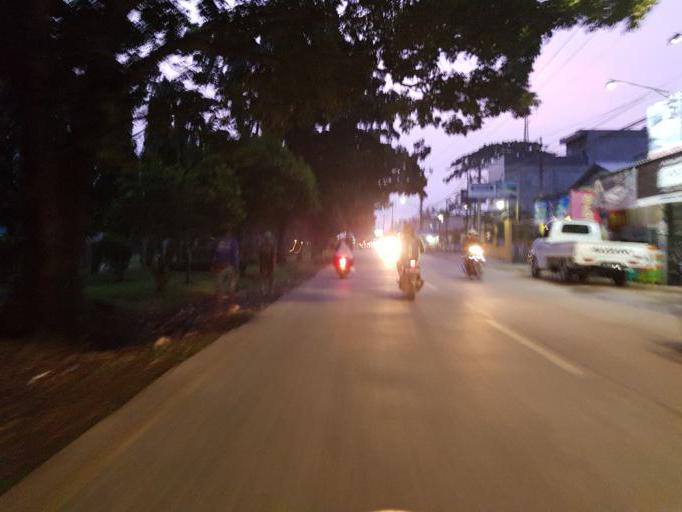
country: ID
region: West Java
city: Serpong
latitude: -6.3251
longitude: 106.6684
